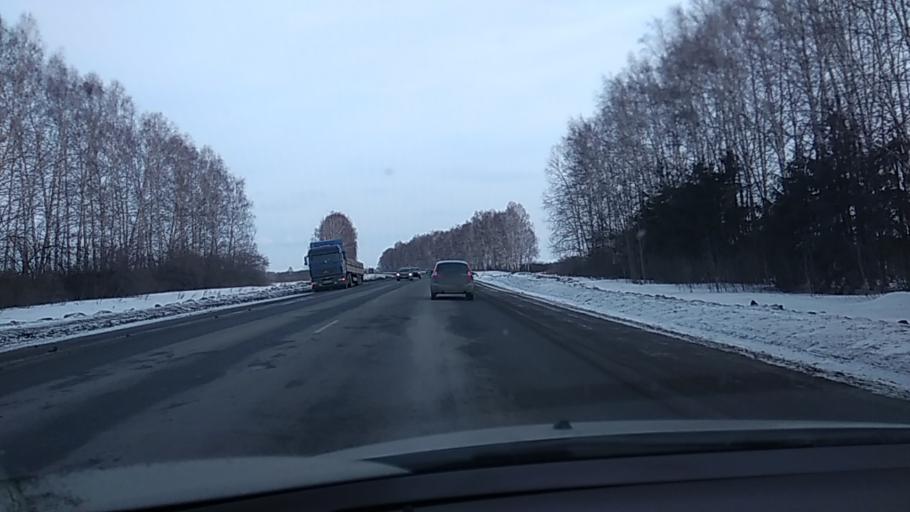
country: RU
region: Sverdlovsk
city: Pokrovskoye
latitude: 56.4668
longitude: 61.6810
